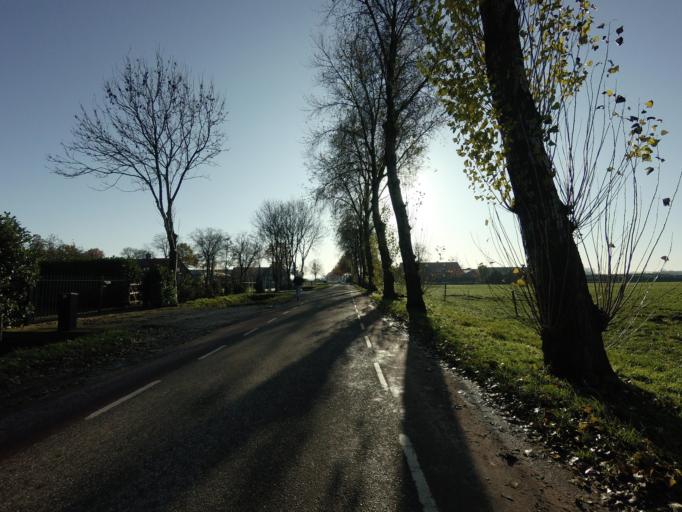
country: NL
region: Gelderland
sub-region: Gemeente Zaltbommel
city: Zaltbommel
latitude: 51.7851
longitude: 5.2741
